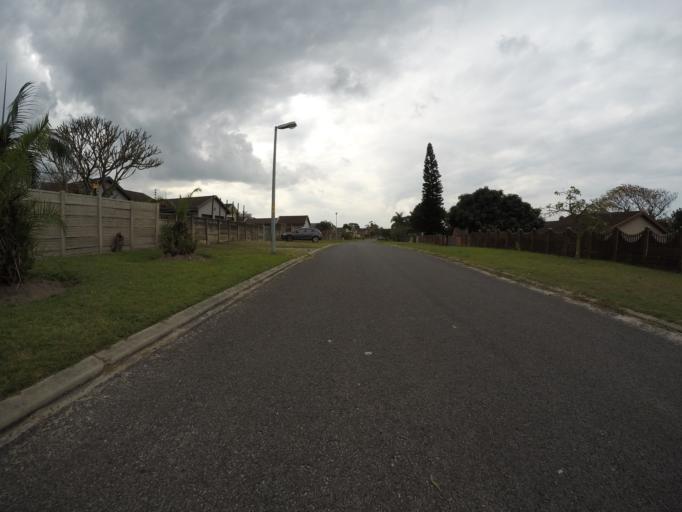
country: ZA
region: KwaZulu-Natal
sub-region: uThungulu District Municipality
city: Richards Bay
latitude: -28.7383
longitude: 32.0517
